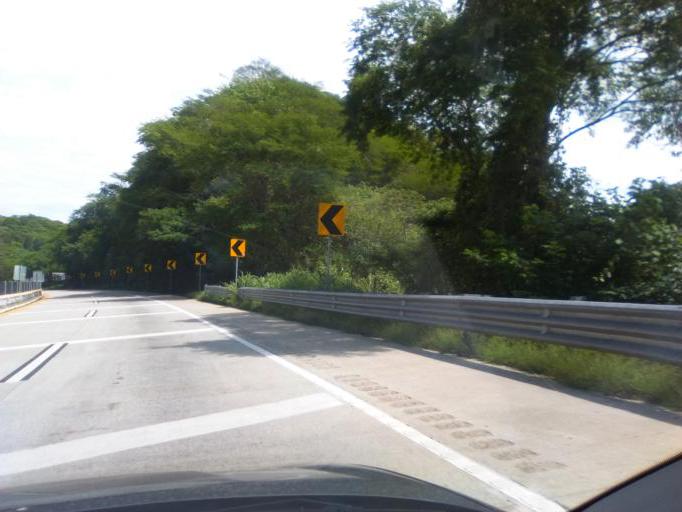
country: MX
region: Guerrero
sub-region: Acapulco de Juarez
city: Pueblo Madero (El Playon)
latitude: 17.0742
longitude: -99.6093
